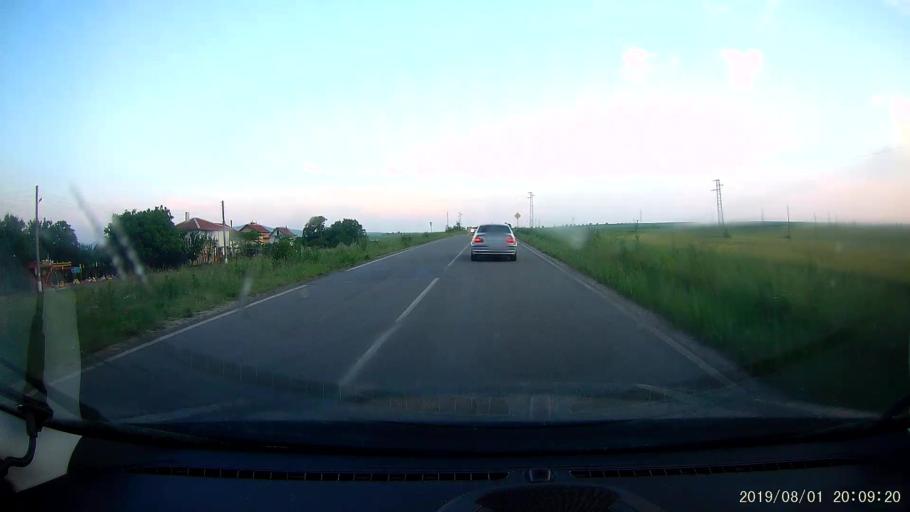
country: BG
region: Yambol
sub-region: Obshtina Yambol
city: Yambol
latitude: 42.4990
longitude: 26.5922
